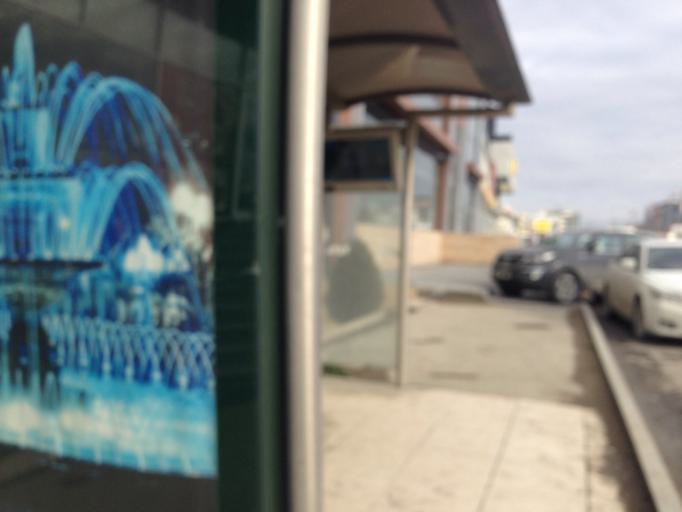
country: AZ
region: Baki
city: Baku
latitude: 40.3894
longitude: 49.8819
